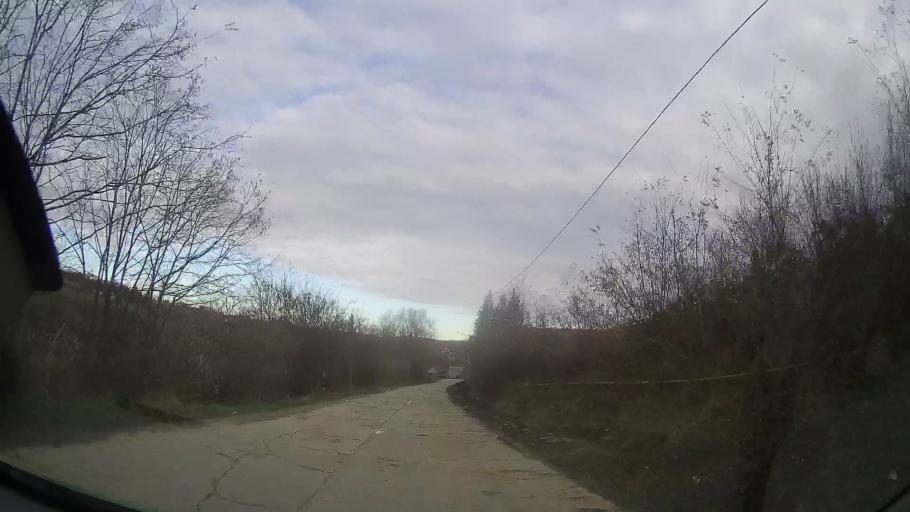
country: RO
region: Bistrita-Nasaud
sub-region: Comuna Sanmihaiu de Campie
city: Sanmihaiu de Campie
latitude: 46.8866
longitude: 24.3325
